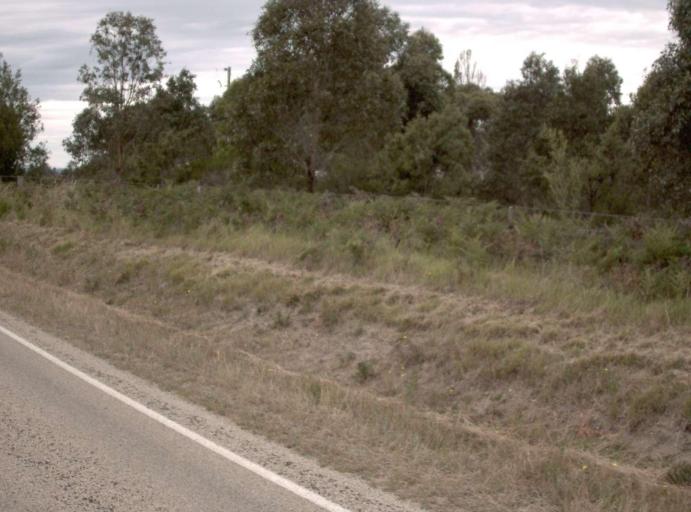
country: AU
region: Victoria
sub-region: East Gippsland
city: Bairnsdale
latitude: -37.9112
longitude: 147.5507
